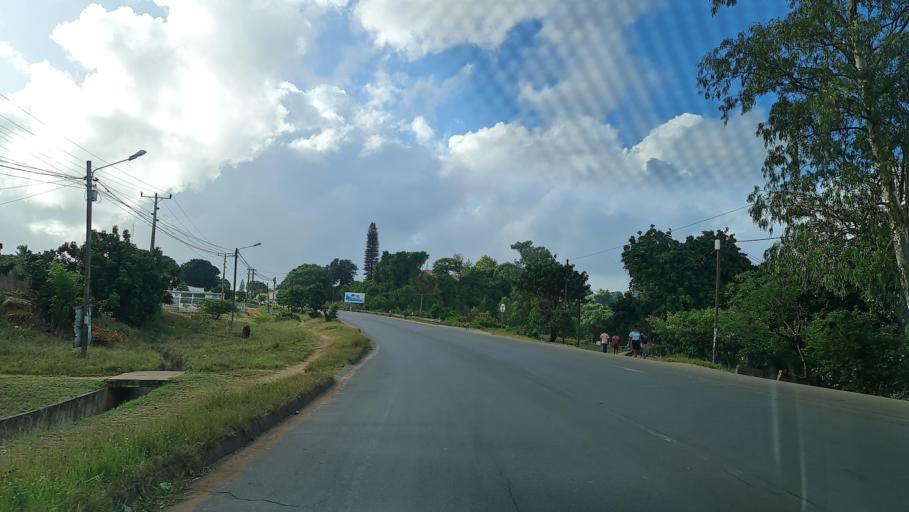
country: MZ
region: Gaza
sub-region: Xai-Xai District
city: Xai-Xai
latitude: -25.0550
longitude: 33.6503
